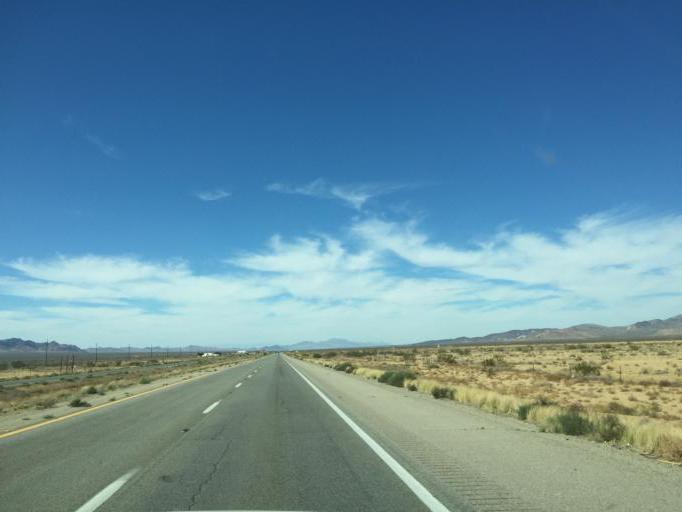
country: US
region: Arizona
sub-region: Mohave County
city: Dolan Springs
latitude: 35.5417
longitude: -114.3605
